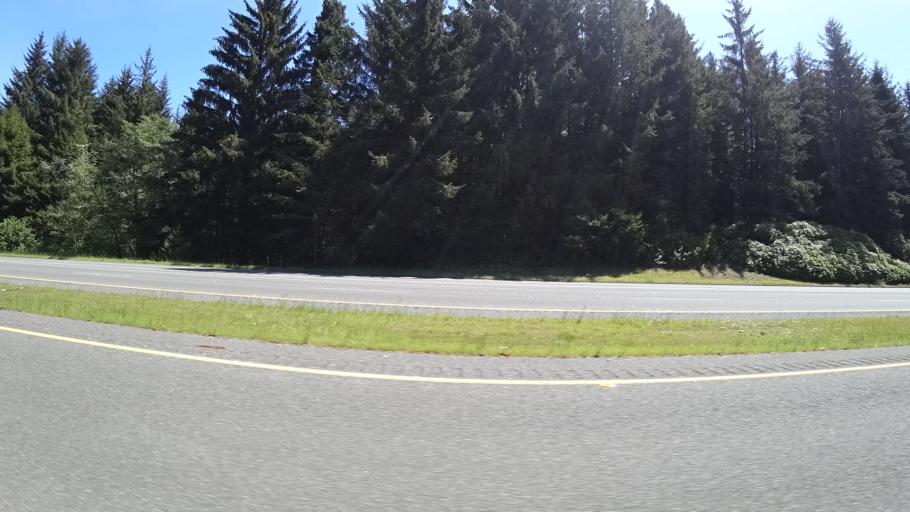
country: US
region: California
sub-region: Humboldt County
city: Westhaven-Moonstone
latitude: 41.1263
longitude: -124.1508
